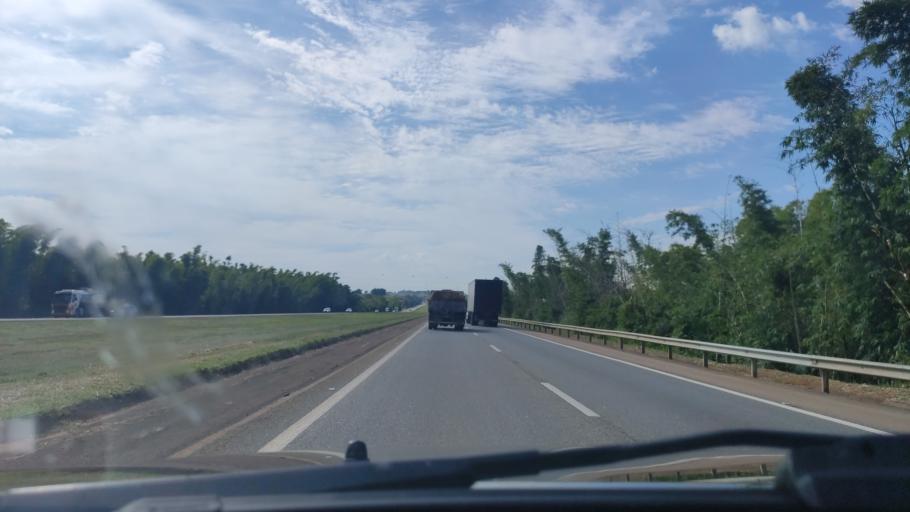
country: BR
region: Sao Paulo
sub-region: Boituva
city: Boituva
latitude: -23.2869
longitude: -47.7654
